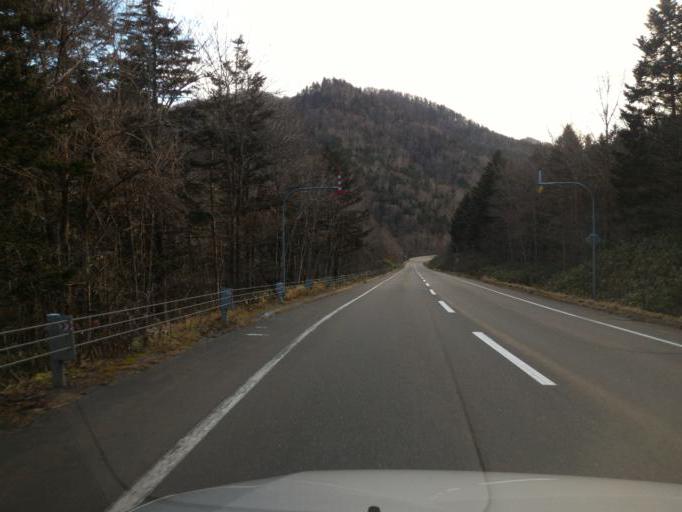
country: JP
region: Hokkaido
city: Shimo-furano
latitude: 43.3638
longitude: 142.2378
